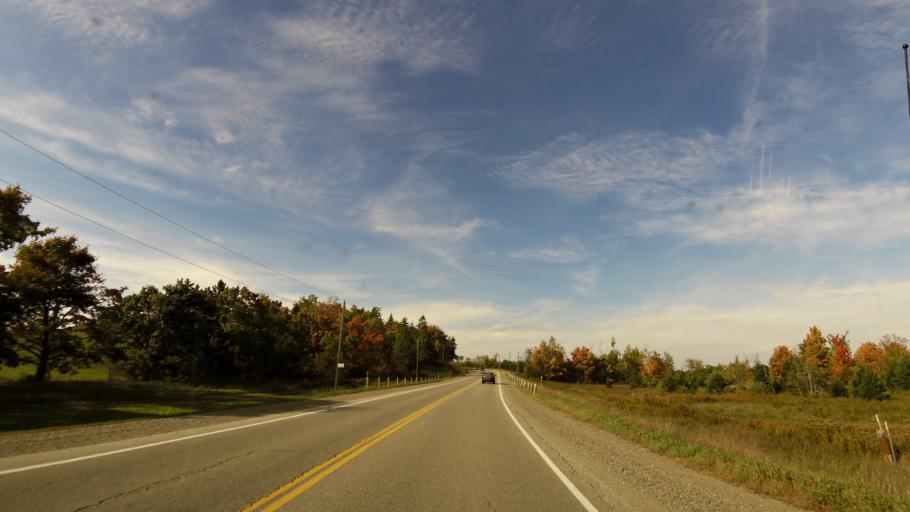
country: CA
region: Ontario
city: Orangeville
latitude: 43.7327
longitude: -80.0608
